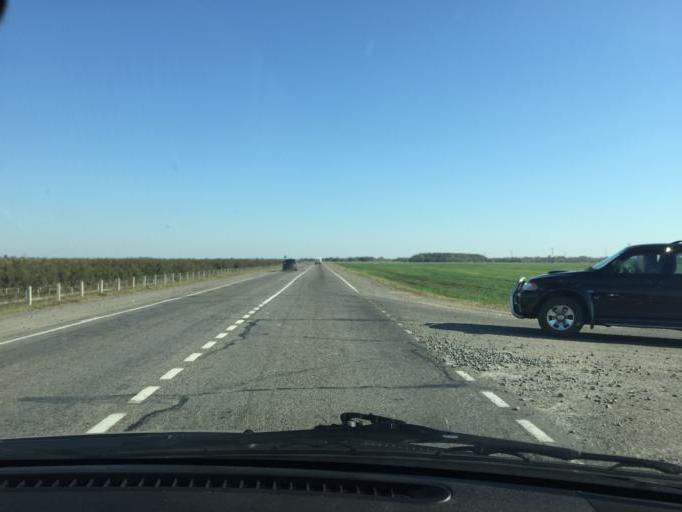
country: BY
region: Gomel
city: Turaw
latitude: 52.0594
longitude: 27.8069
